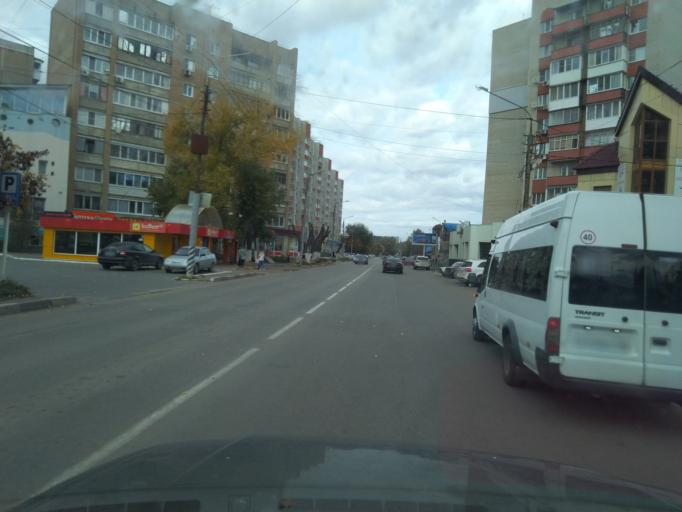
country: RU
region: Saratov
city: Engel's
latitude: 51.4897
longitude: 46.1226
